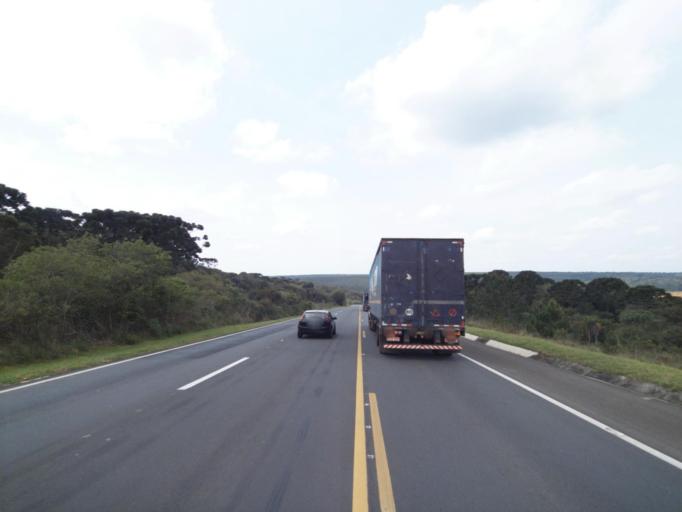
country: BR
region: Parana
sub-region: Irati
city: Irati
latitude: -25.4584
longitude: -50.4597
